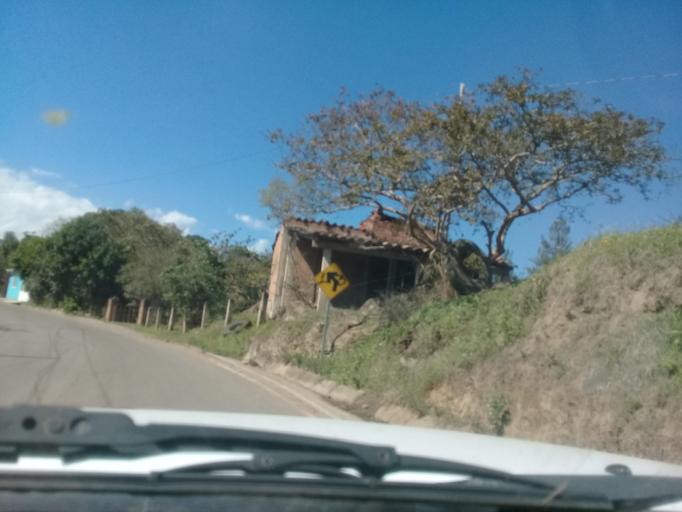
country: MX
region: Veracruz
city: El Castillo
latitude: 19.5489
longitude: -96.8505
